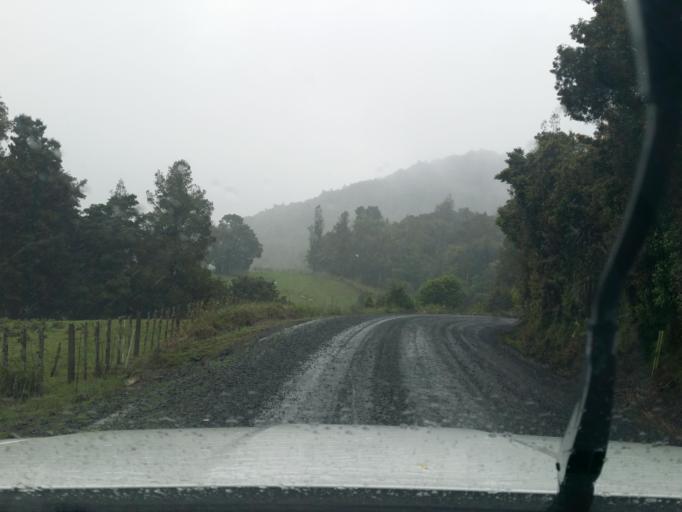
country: NZ
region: Northland
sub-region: Kaipara District
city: Dargaville
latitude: -35.7460
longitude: 173.9620
